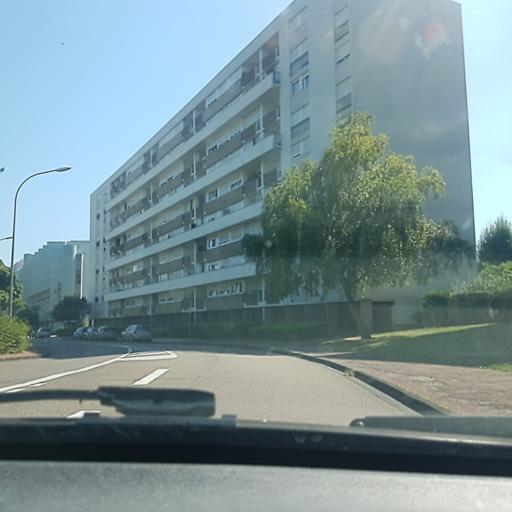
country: FR
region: Bourgogne
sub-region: Departement de Saone-et-Loire
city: Chalon-sur-Saone
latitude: 46.7890
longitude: 4.8417
